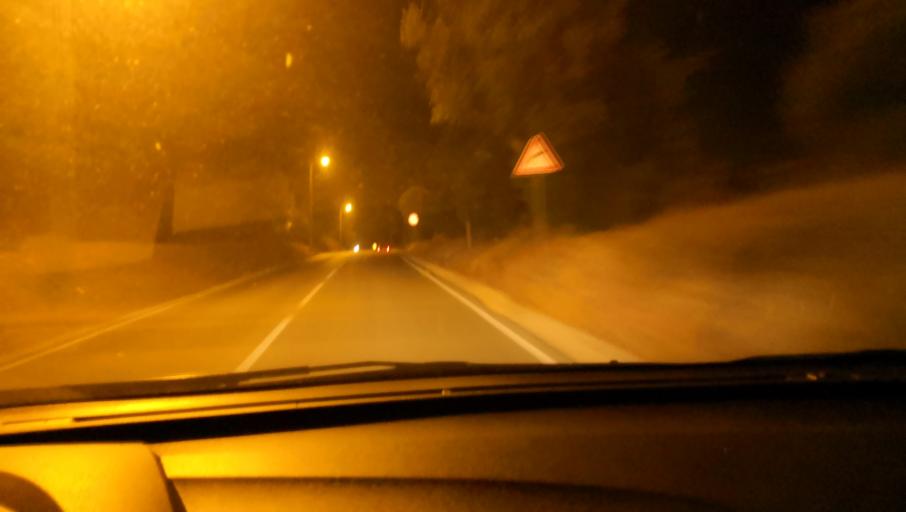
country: PT
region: Setubal
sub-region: Palmela
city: Palmela
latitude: 38.5616
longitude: -8.8926
